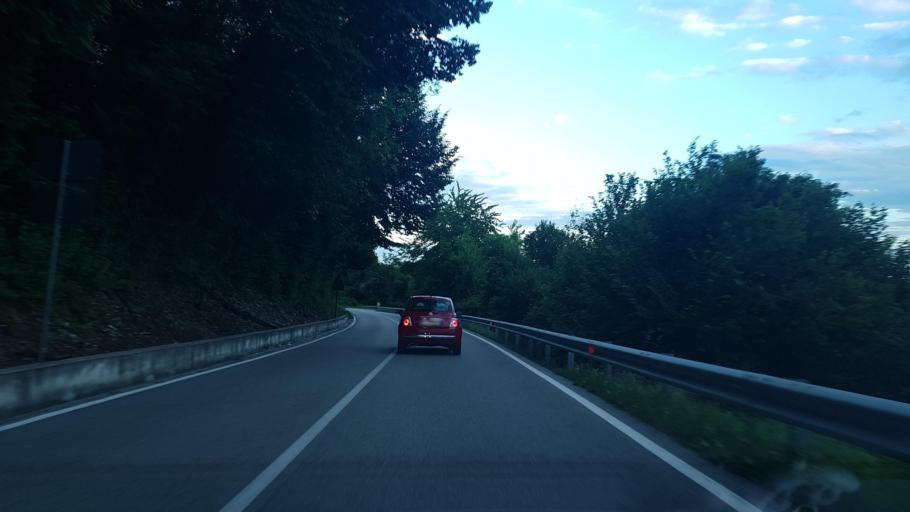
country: IT
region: Friuli Venezia Giulia
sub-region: Provincia di Pordenone
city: Pinzano al Tagliamento
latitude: 46.1819
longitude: 12.9596
